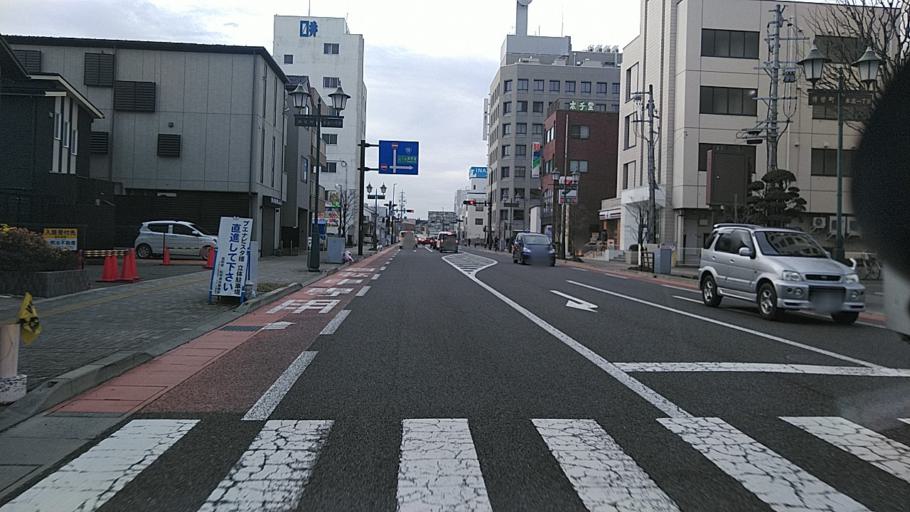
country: JP
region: Nagano
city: Matsumoto
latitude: 36.2283
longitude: 137.9695
